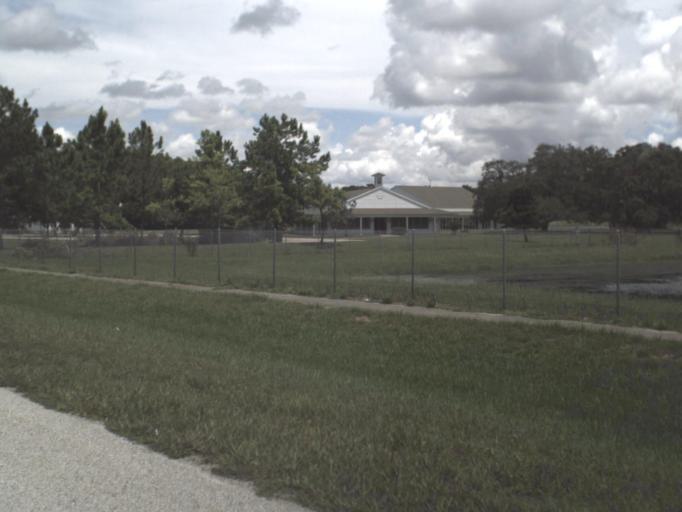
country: US
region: Florida
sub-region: Pasco County
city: Trinity
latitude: 28.1538
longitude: -82.6958
